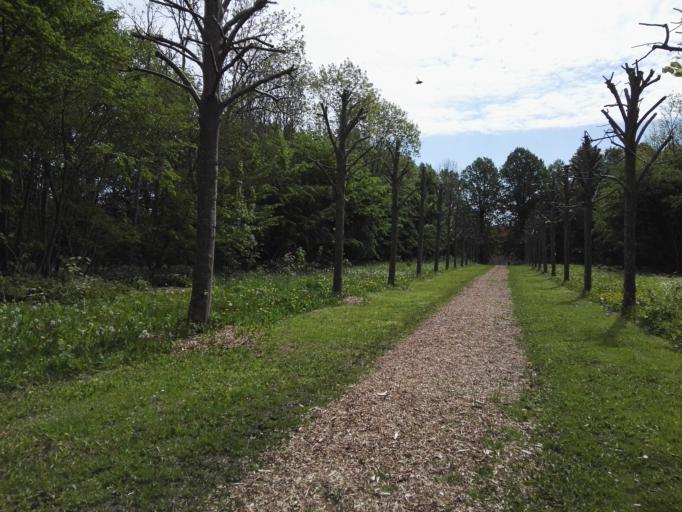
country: DK
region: Capital Region
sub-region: Frederikssund Kommune
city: Skibby
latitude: 55.7421
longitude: 12.0077
